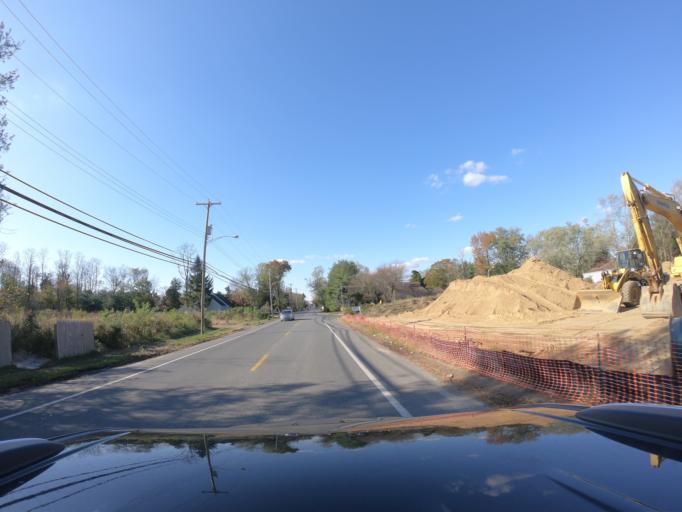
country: US
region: New Jersey
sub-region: Monmouth County
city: Ramtown
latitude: 40.0976
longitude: -74.1641
